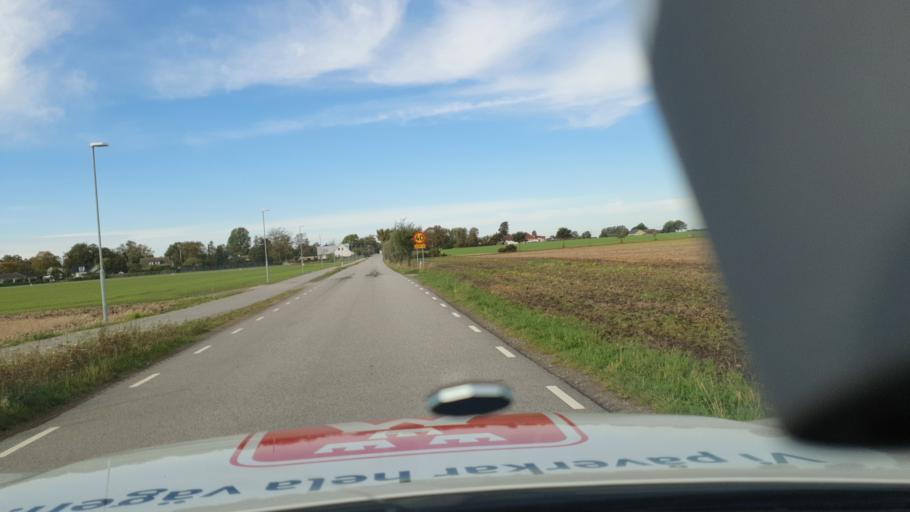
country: SE
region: Skane
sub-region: Malmo
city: Bunkeflostrand
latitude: 55.5001
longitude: 12.9649
